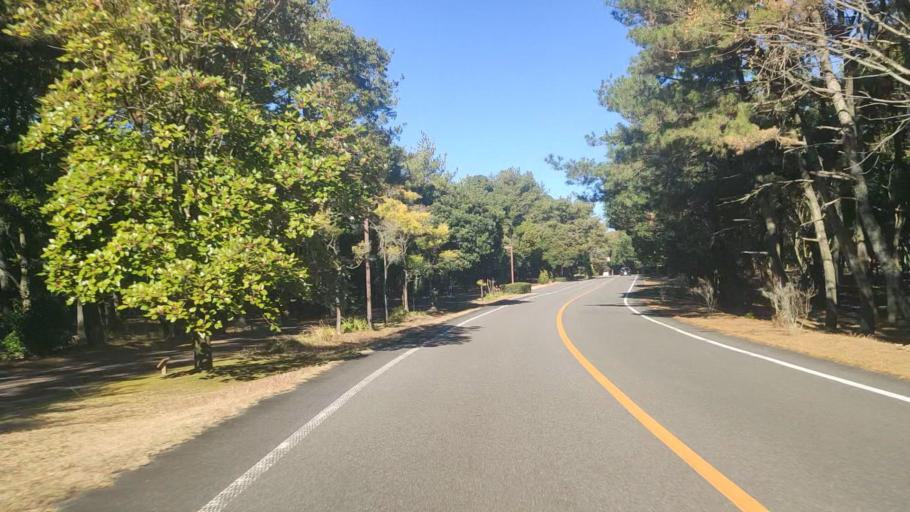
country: JP
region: Miyazaki
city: Miyazaki-shi
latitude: 31.9464
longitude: 131.4648
